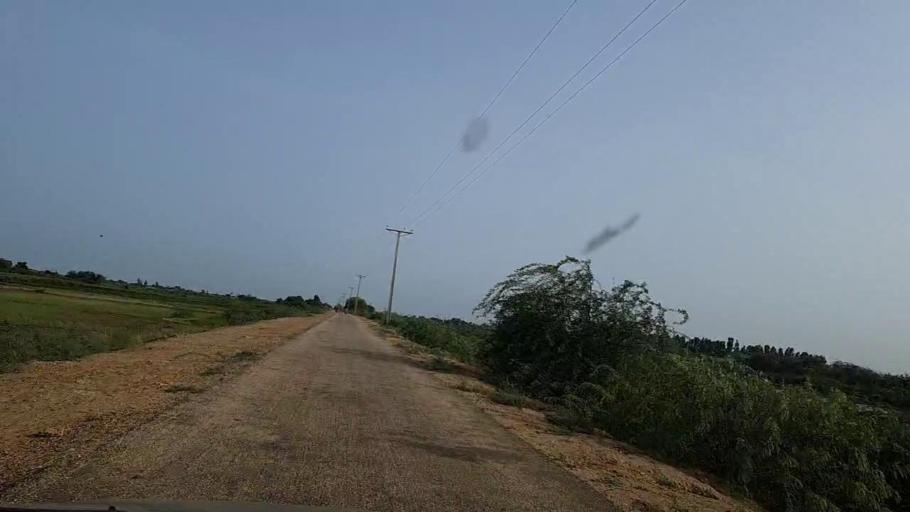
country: PK
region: Sindh
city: Kotri
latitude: 25.2064
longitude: 68.2566
